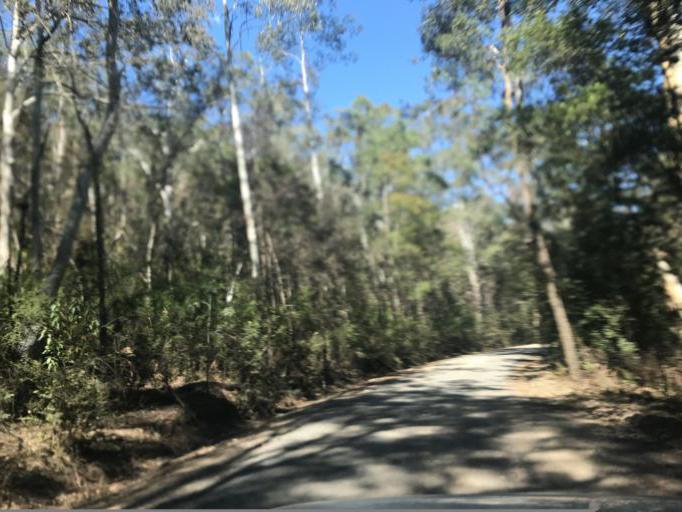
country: AU
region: New South Wales
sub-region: Wyong Shire
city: Little Jilliby
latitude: -33.1677
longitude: 151.0689
